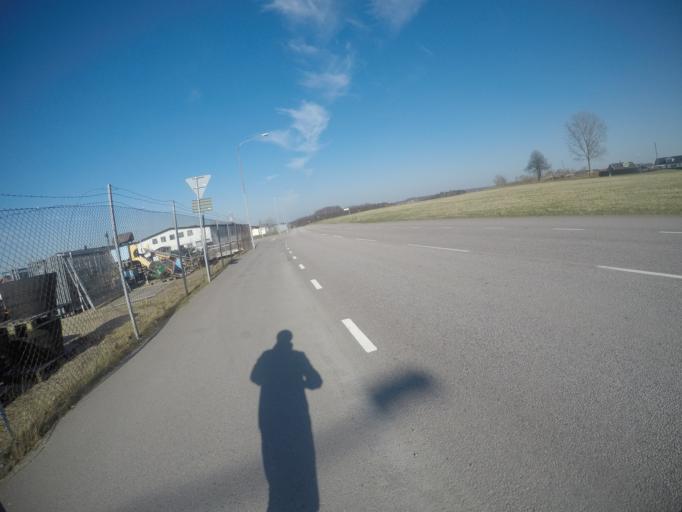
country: SE
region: Halland
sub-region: Laholms Kommun
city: Laholm
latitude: 56.5075
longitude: 13.0580
